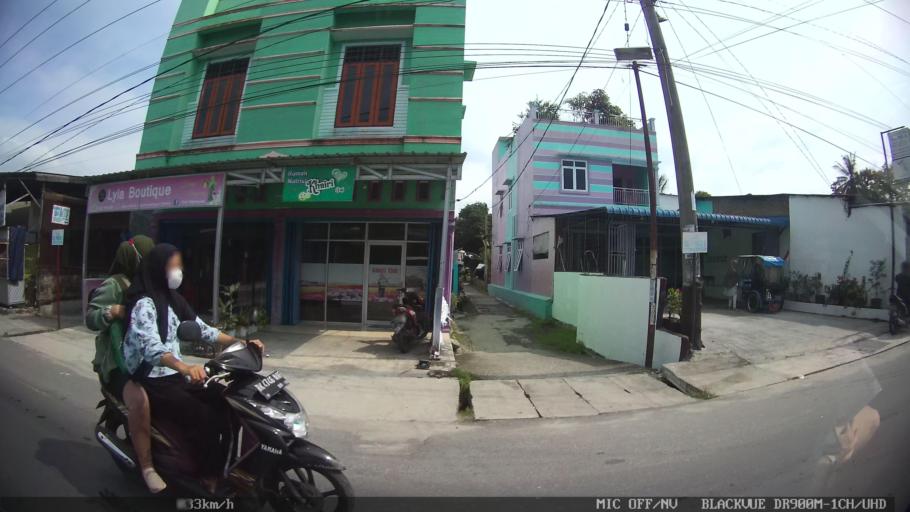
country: ID
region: North Sumatra
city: Percut
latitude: 3.6121
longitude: 98.8091
